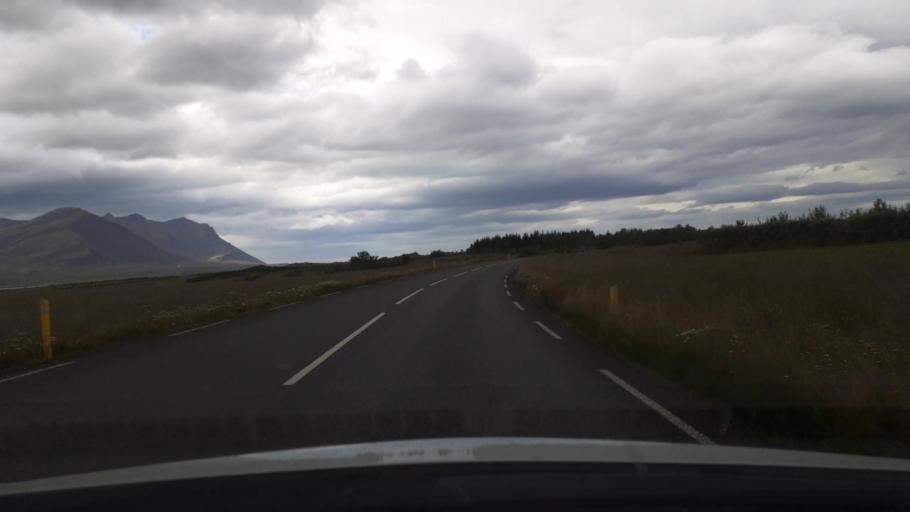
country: IS
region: West
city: Borgarnes
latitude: 64.5597
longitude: -21.7465
